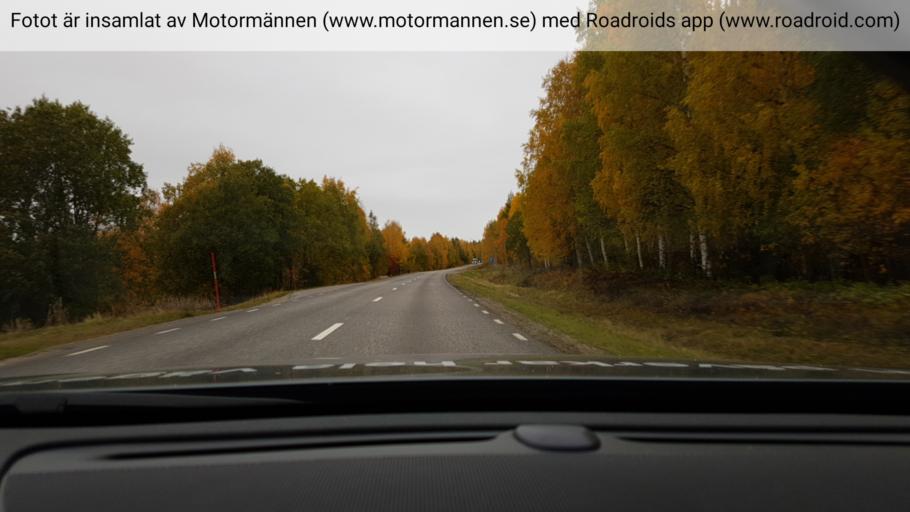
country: SE
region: Norrbotten
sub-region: Overkalix Kommun
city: OEverkalix
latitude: 66.5392
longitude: 22.7541
